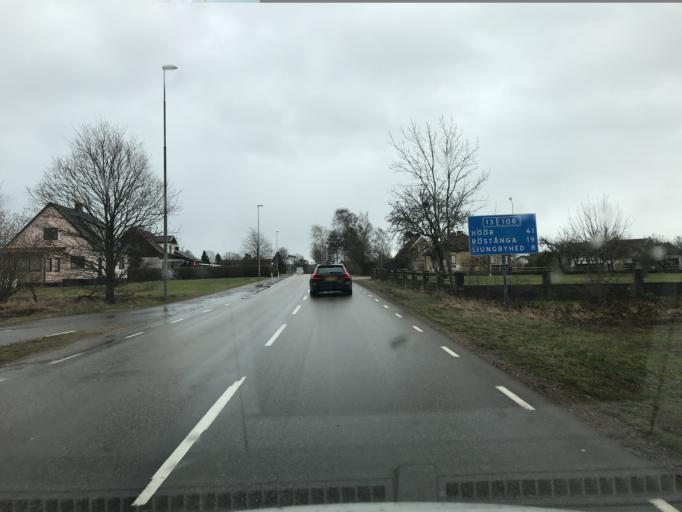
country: SE
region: Skane
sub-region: Klippans Kommun
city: Klippan
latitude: 56.1200
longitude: 13.1731
